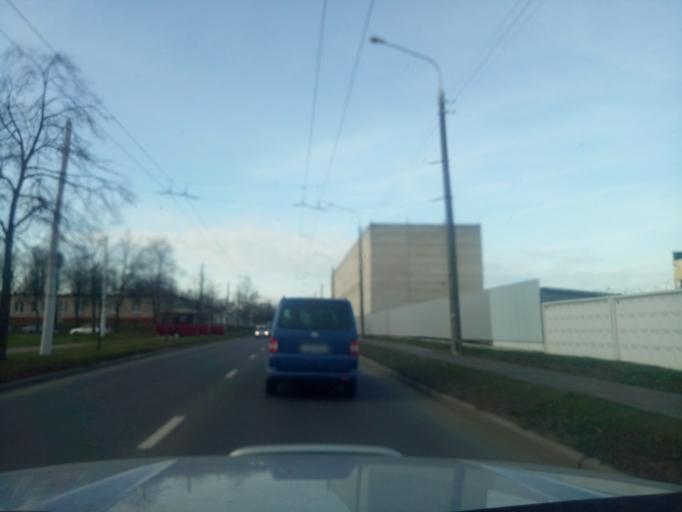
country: BY
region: Minsk
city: Novoye Medvezhino
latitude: 53.8846
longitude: 27.4959
